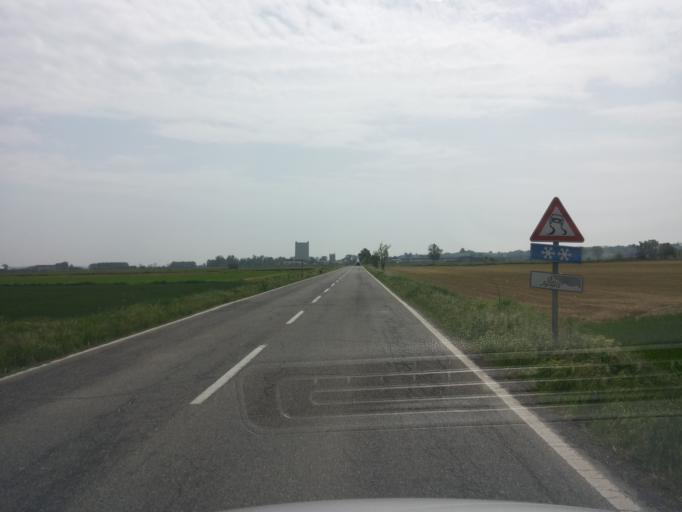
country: IT
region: Piedmont
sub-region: Provincia di Alessandria
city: Terruggia
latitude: 45.0829
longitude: 8.4743
